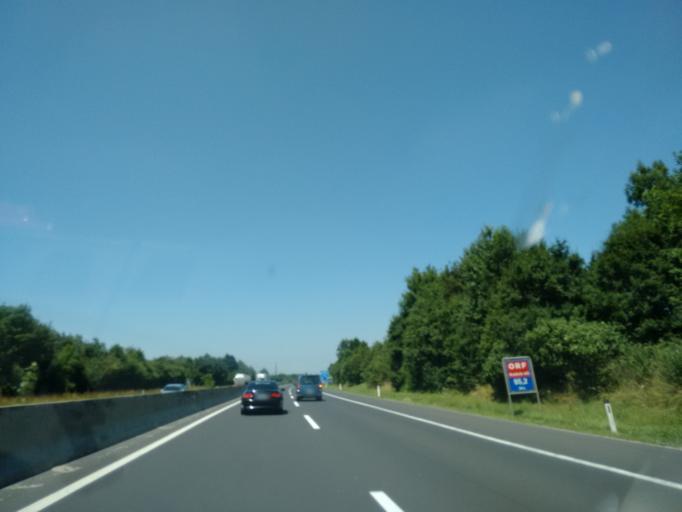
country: AT
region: Upper Austria
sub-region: Wels-Land
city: Gunskirchen
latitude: 48.1583
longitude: 13.9790
